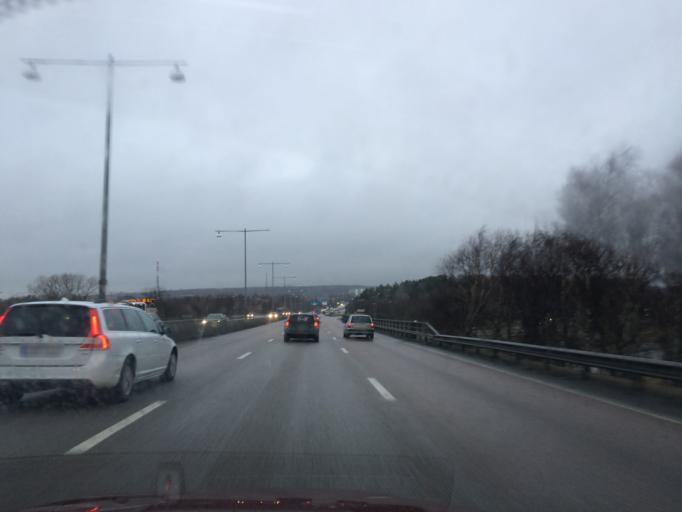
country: SE
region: Vaestra Goetaland
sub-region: Goteborg
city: Majorna
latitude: 57.6975
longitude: 11.8971
